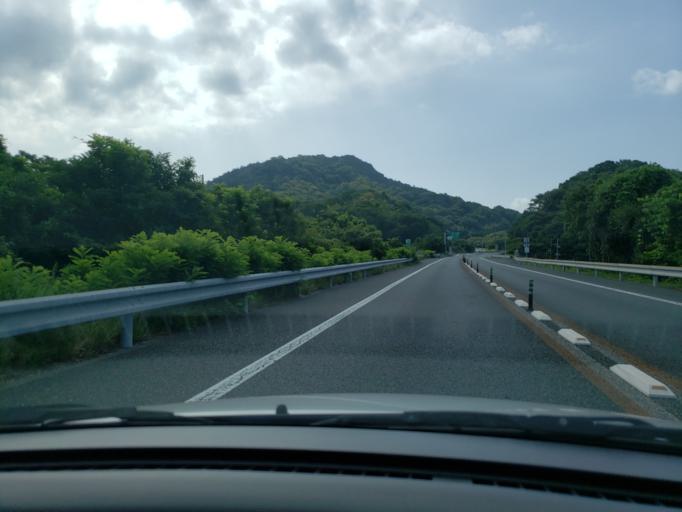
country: JP
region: Hiroshima
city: Innoshima
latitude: 34.2091
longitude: 133.0751
